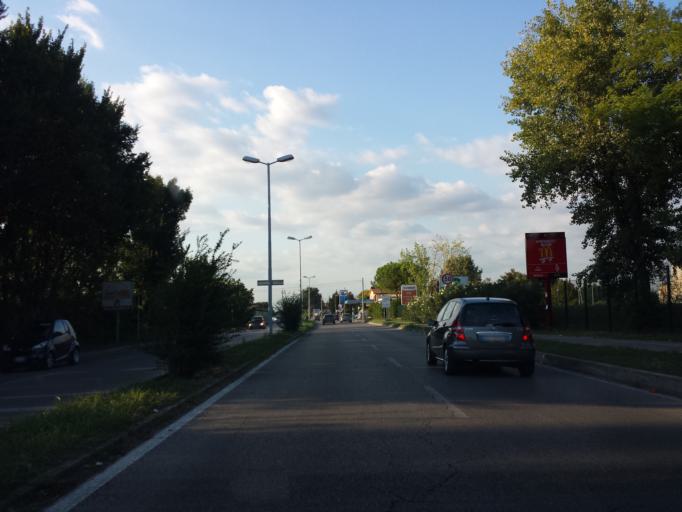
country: IT
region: Veneto
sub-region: Provincia di Padova
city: Padova
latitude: 45.4257
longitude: 11.9004
